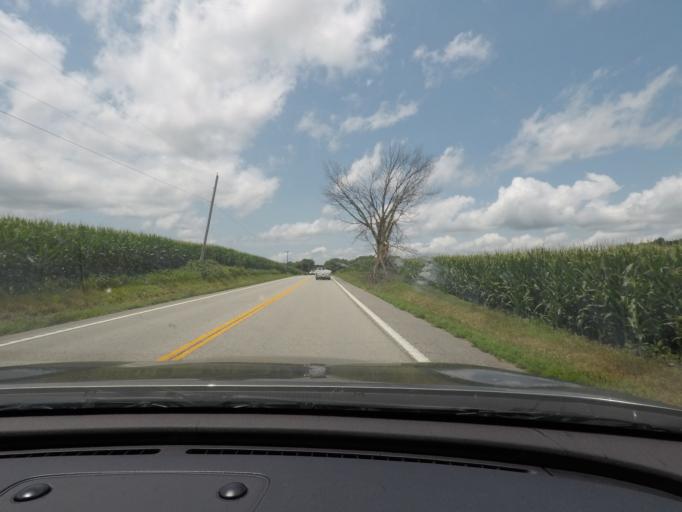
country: US
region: Missouri
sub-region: Carroll County
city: Carrollton
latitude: 39.1979
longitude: -93.4313
